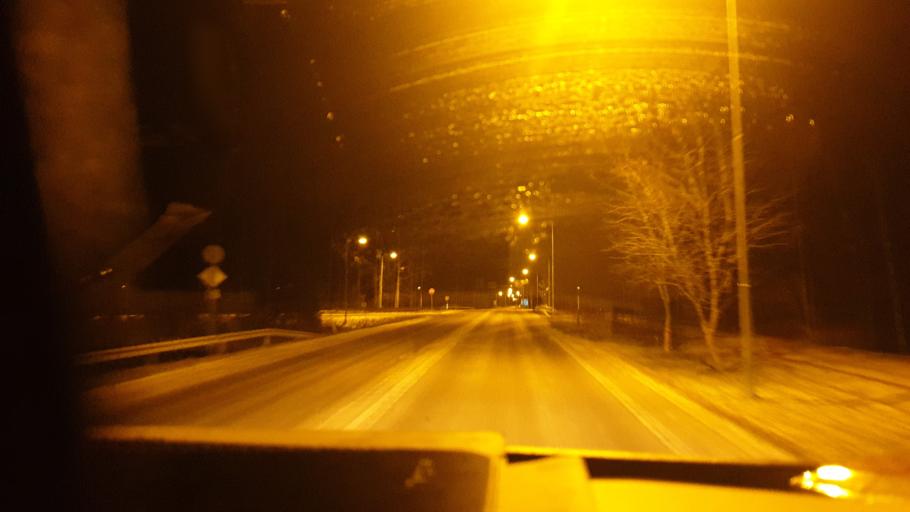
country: FI
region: Southern Ostrobothnia
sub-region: Kuusiokunnat
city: Alavus
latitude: 62.5933
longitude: 23.6145
